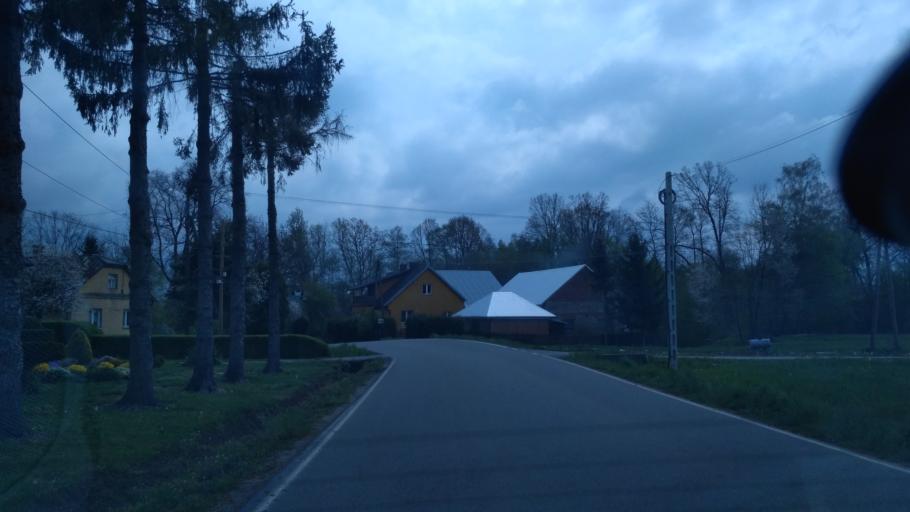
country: PL
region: Subcarpathian Voivodeship
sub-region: Powiat brzozowski
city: Haczow
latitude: 49.6486
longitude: 21.9148
